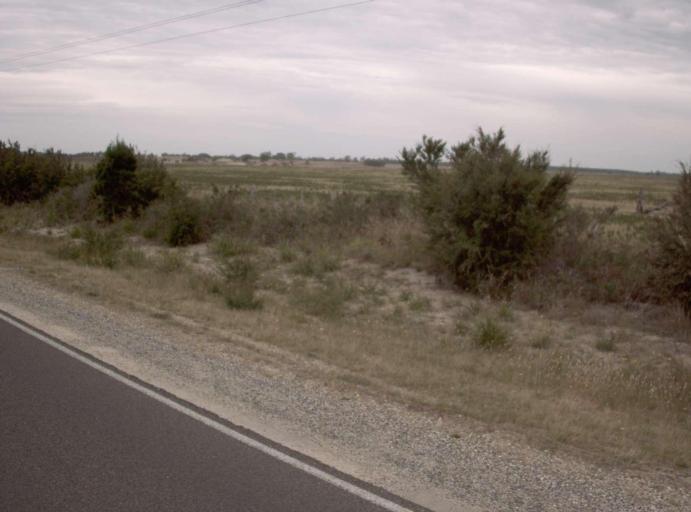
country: AU
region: Victoria
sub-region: Wellington
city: Sale
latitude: -38.1836
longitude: 147.2627
